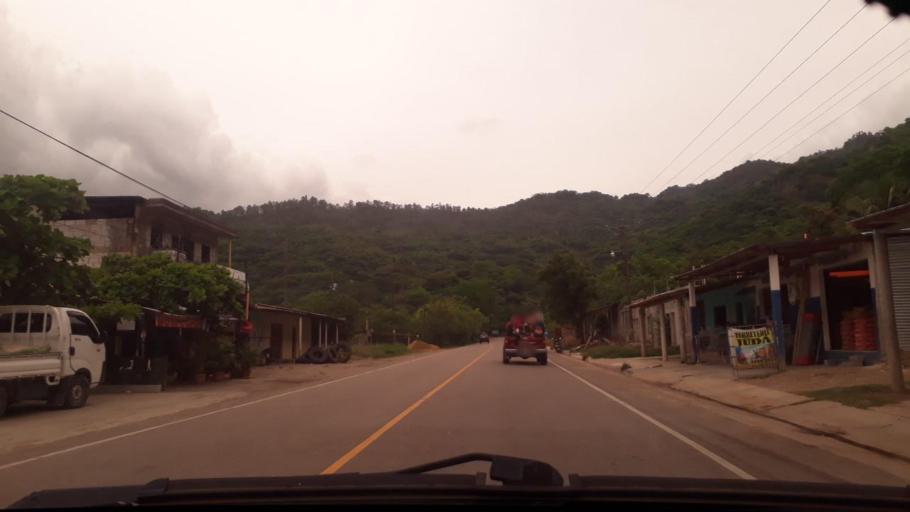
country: GT
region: Chiquimula
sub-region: Municipio de Camotan
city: Camotan
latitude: 14.8268
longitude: -89.3524
